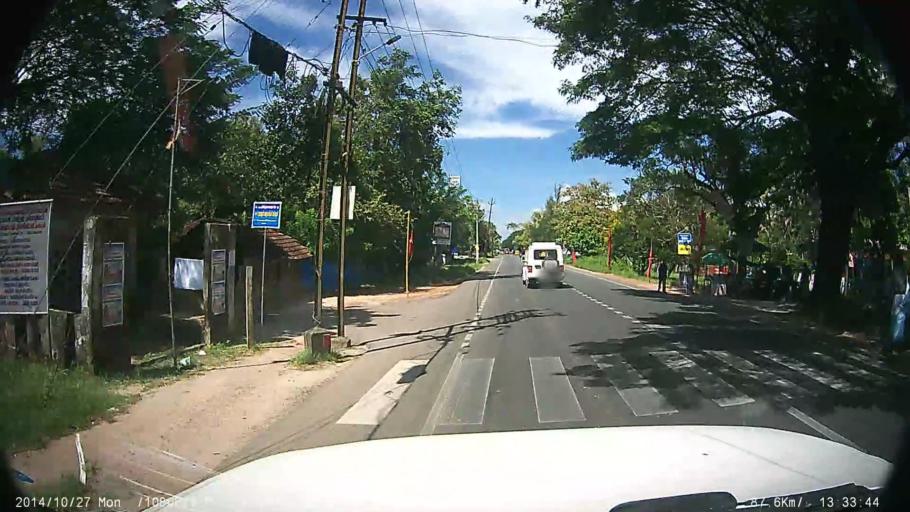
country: IN
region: Kerala
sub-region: Alappuzha
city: Alleppey
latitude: 9.5775
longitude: 76.3274
